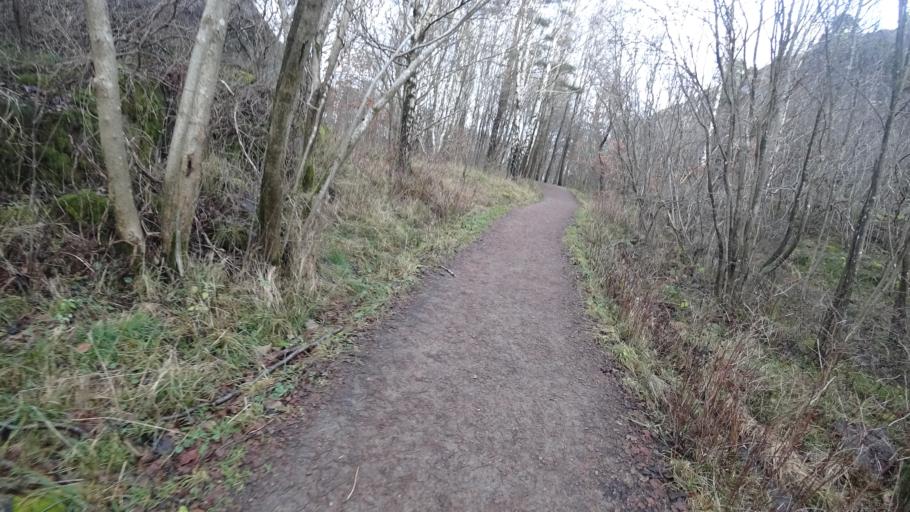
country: SE
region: Vaestra Goetaland
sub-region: Goteborg
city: Majorna
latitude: 57.6669
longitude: 11.9466
